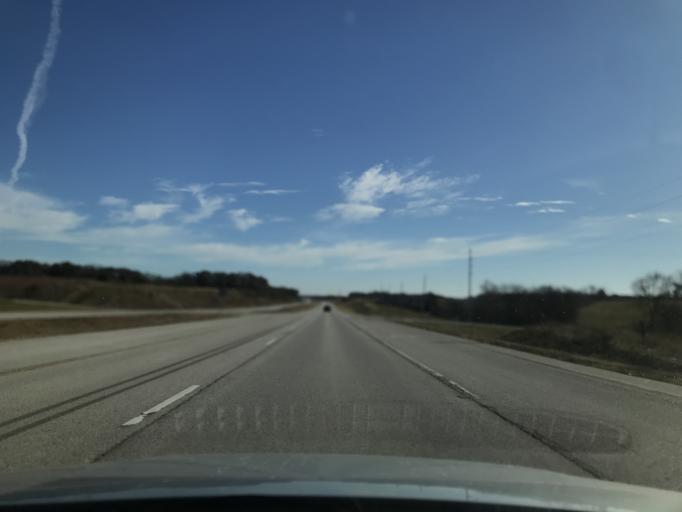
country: US
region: Illinois
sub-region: Hancock County
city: Carthage
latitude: 40.4145
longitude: -91.0354
